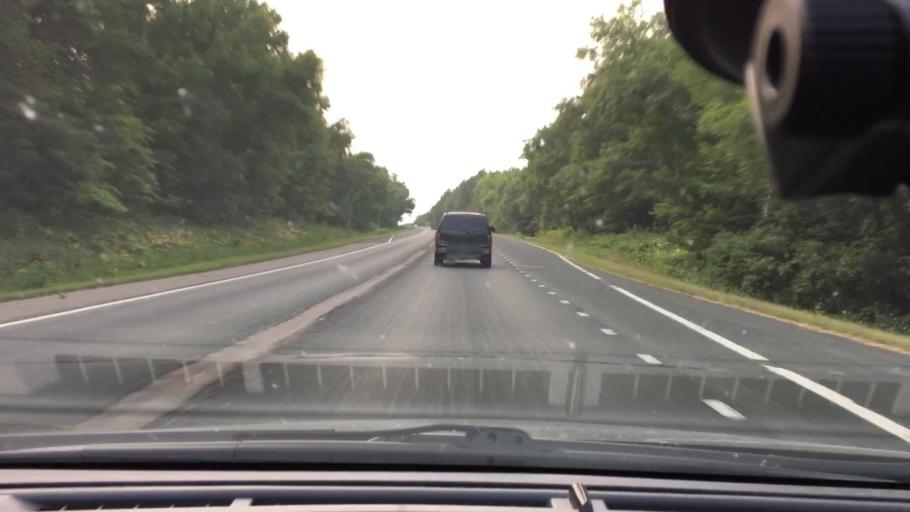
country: US
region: Minnesota
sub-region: Mille Lacs County
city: Vineland
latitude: 46.2377
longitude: -93.8017
